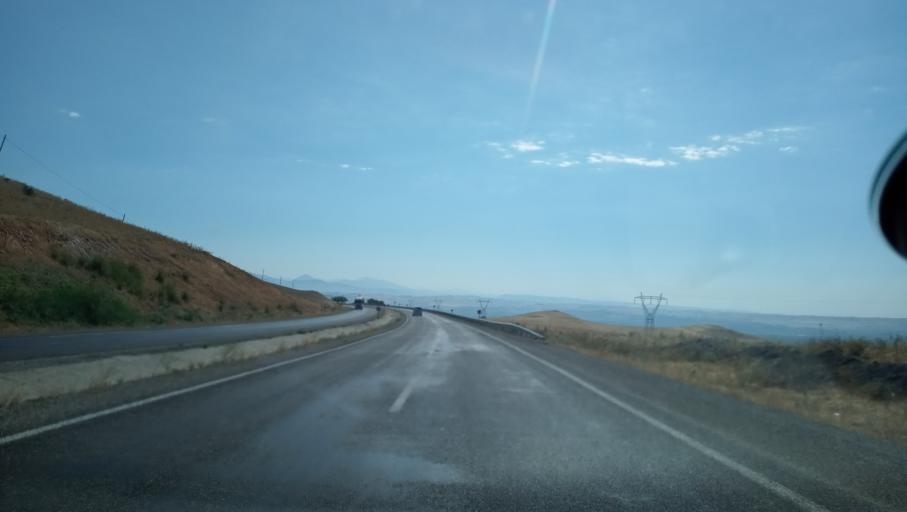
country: TR
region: Diyarbakir
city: Malabadi
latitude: 38.1182
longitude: 41.1413
